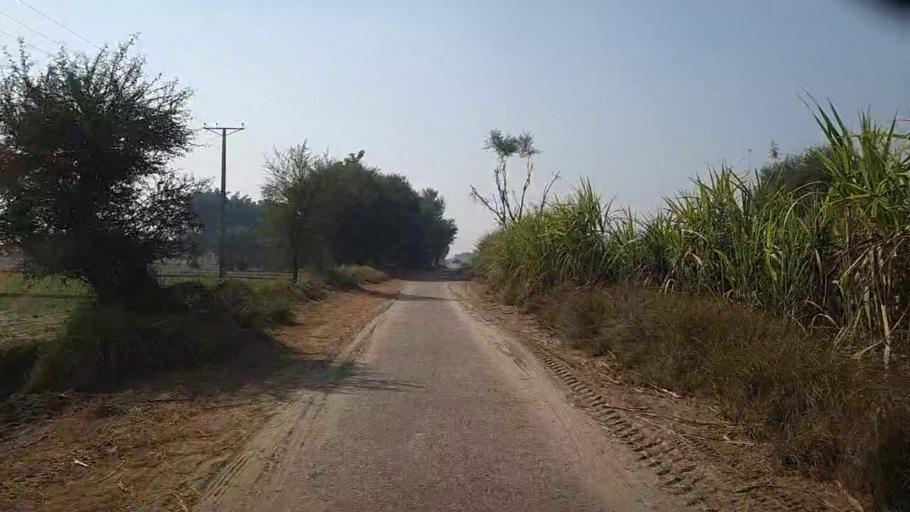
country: PK
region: Sindh
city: Bozdar
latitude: 27.2645
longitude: 68.6226
